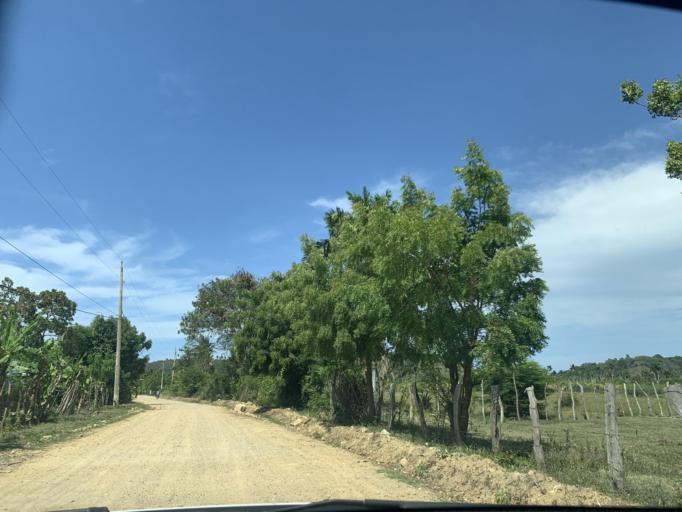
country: DO
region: Puerto Plata
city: Luperon
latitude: 19.8942
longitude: -70.8824
